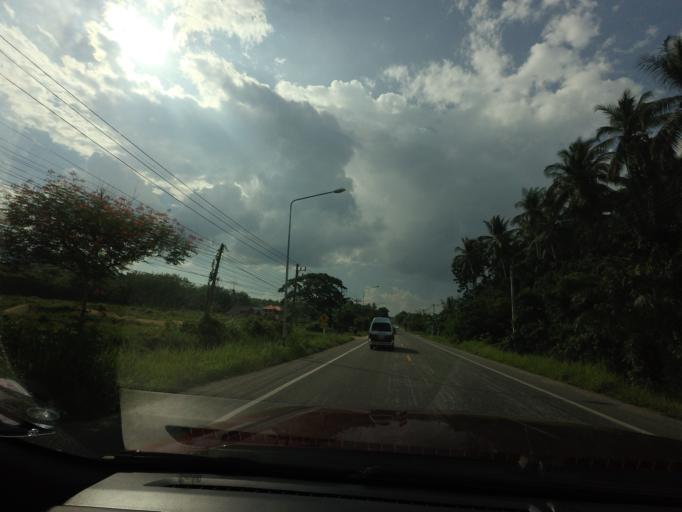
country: TH
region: Pattani
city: Mae Lan
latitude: 6.5967
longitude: 101.1947
